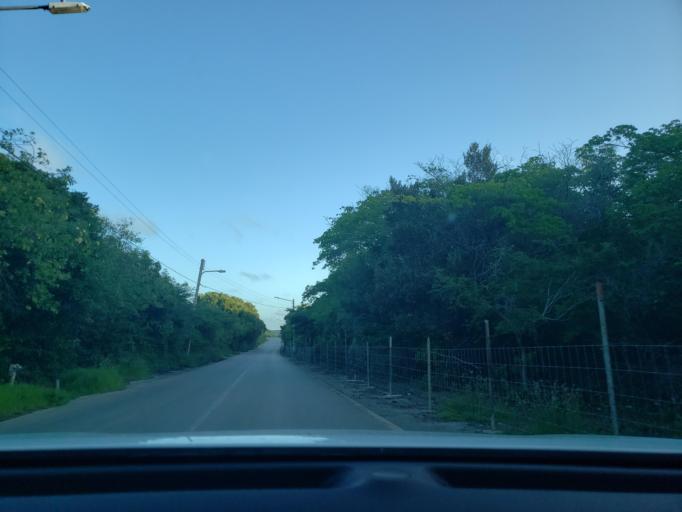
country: CW
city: Barber
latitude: 12.2665
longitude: -69.0660
